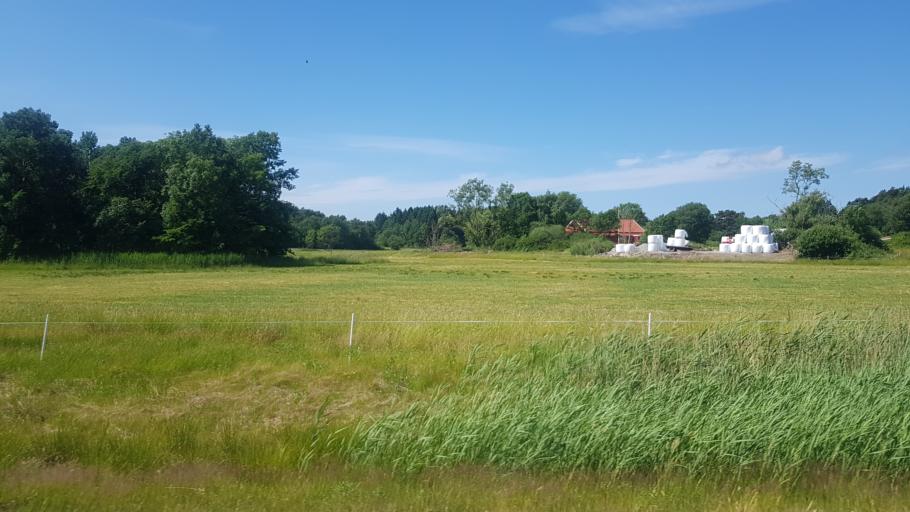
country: SE
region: Vaestra Goetaland
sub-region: Tjorns Kommun
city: Skaerhamn
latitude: 58.0076
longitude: 11.6101
